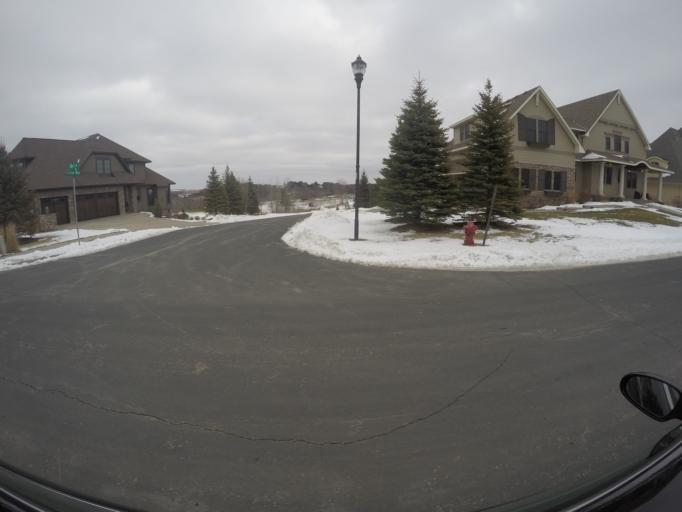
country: US
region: Minnesota
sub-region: Hennepin County
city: Eden Prairie
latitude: 44.8254
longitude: -93.4905
